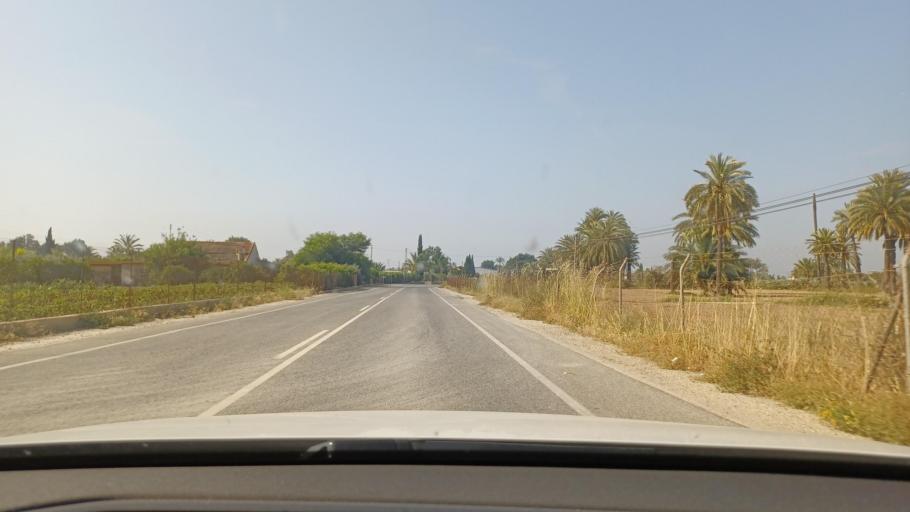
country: ES
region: Valencia
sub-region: Provincia de Alicante
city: Elche
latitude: 38.2281
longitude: -0.7181
